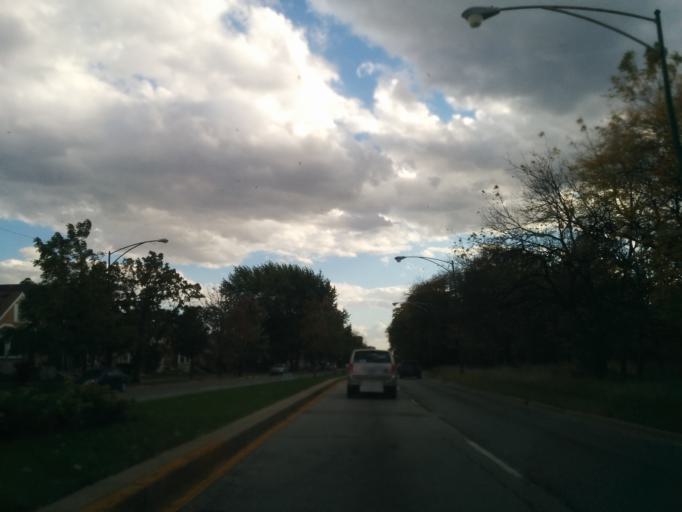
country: US
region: Illinois
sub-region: Cook County
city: Norridge
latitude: 41.9481
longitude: -87.8366
